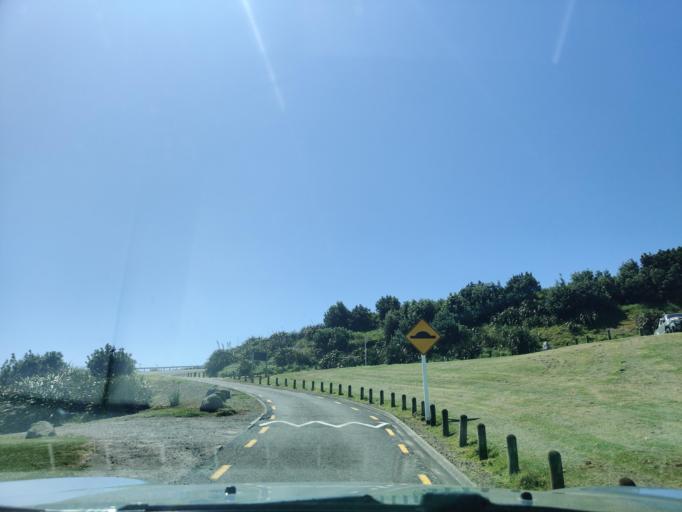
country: NZ
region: Taranaki
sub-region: South Taranaki District
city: Hawera
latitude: -39.6052
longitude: 174.2421
